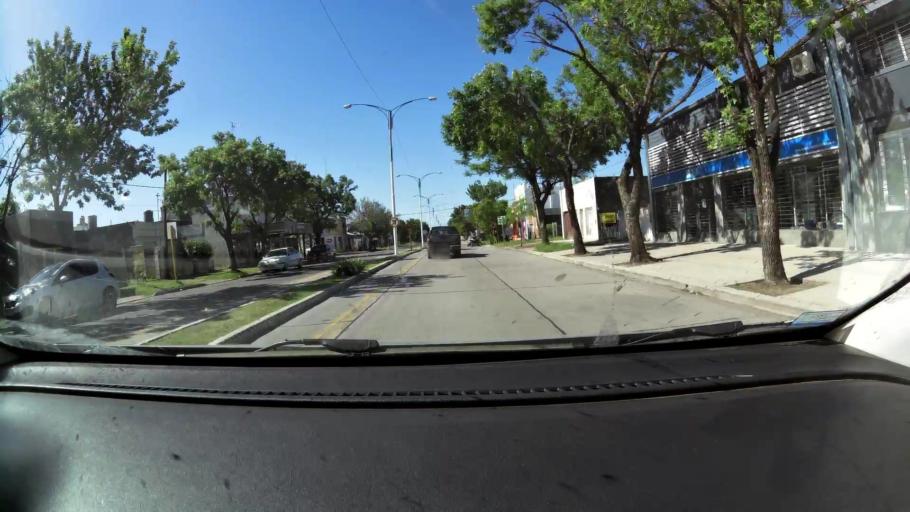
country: AR
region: Santa Fe
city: Rafaela
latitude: -31.2422
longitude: -61.4893
